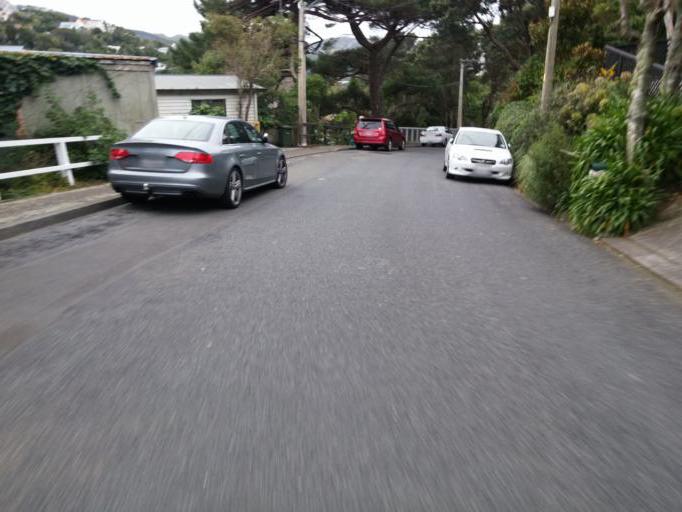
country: NZ
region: Wellington
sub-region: Wellington City
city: Kelburn
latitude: -41.2891
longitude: 174.7549
